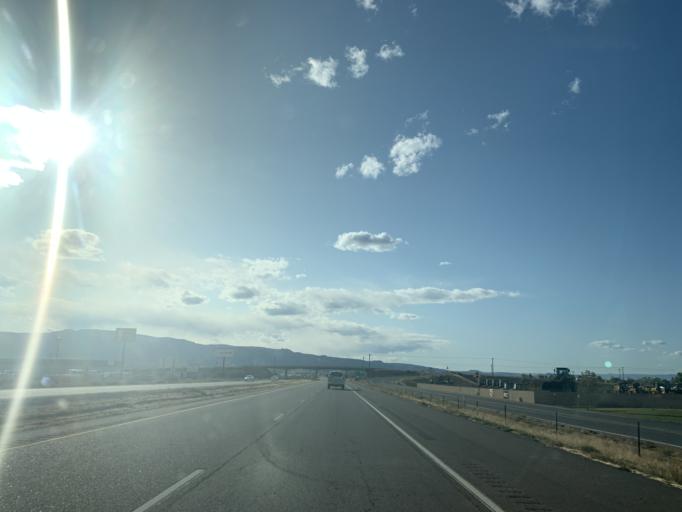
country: US
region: Colorado
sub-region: Mesa County
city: Redlands
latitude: 39.1141
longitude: -108.6233
